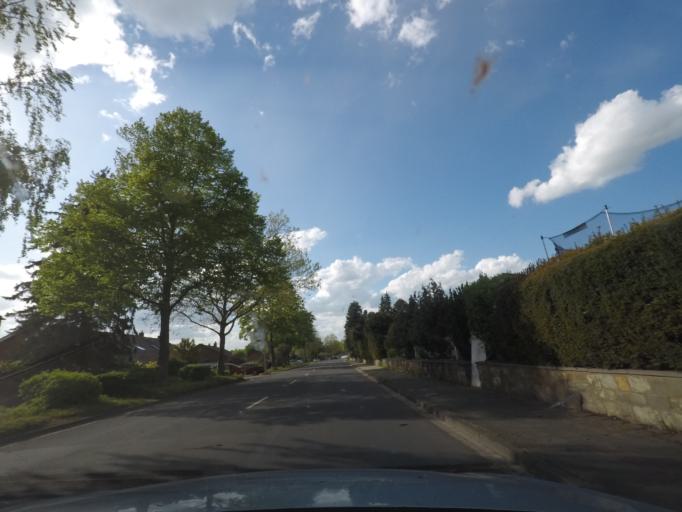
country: DE
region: Lower Saxony
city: Helmstedt
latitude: 52.2258
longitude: 11.0301
